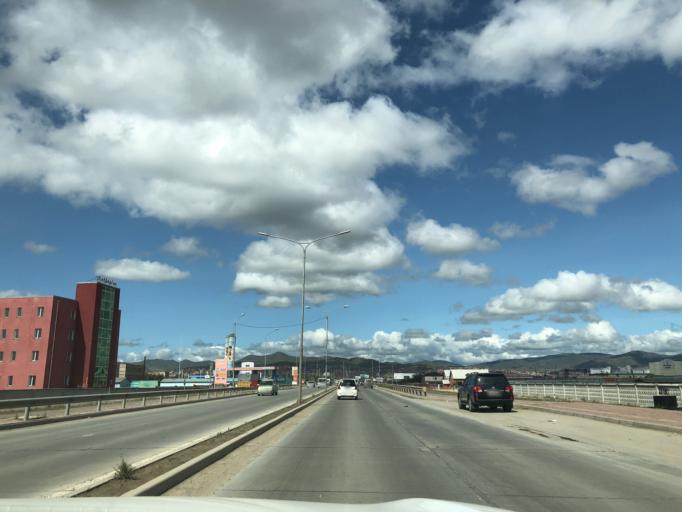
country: MN
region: Ulaanbaatar
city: Ulaanbaatar
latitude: 47.8924
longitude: 106.7854
